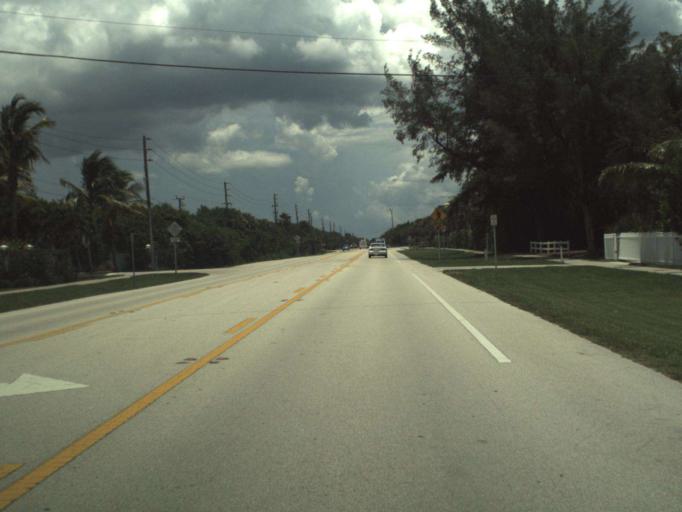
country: US
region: Florida
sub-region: Martin County
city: Sewall's Point
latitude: 27.2340
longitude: -80.1860
